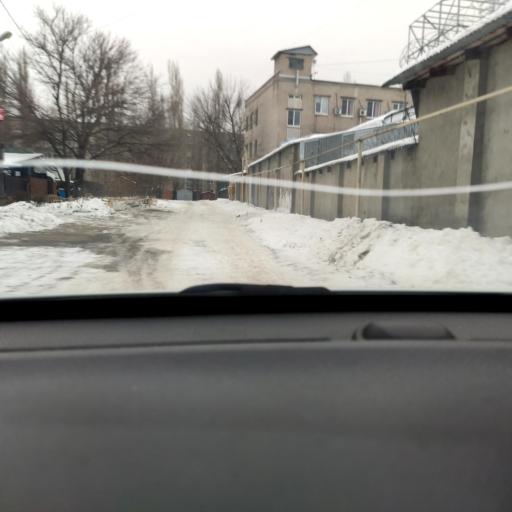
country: RU
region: Voronezj
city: Somovo
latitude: 51.7429
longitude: 39.3582
